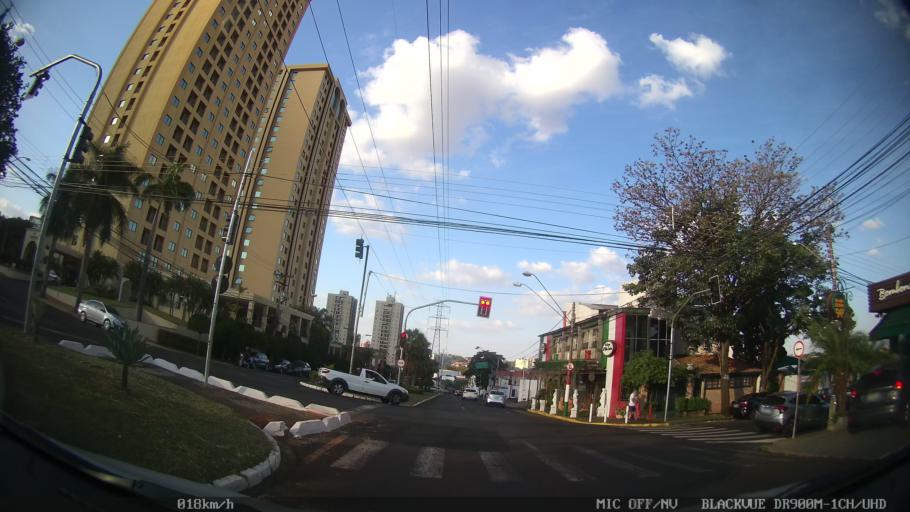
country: BR
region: Sao Paulo
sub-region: Ribeirao Preto
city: Ribeirao Preto
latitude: -21.1942
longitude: -47.8023
